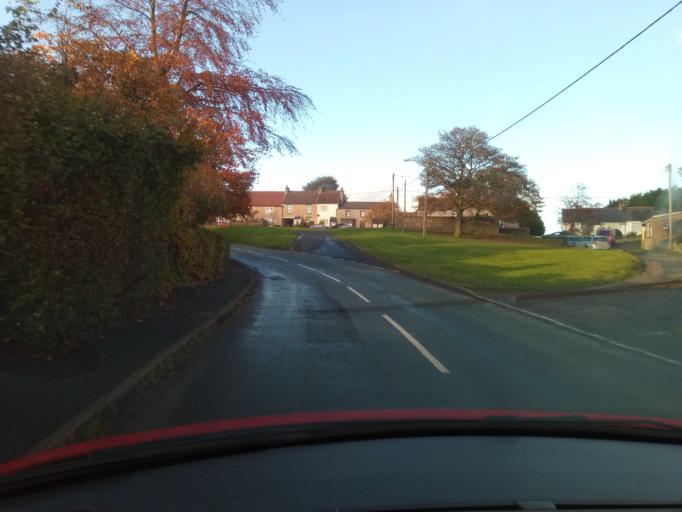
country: GB
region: England
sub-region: County Durham
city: Hamsterley
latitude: 54.6734
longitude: -1.8146
